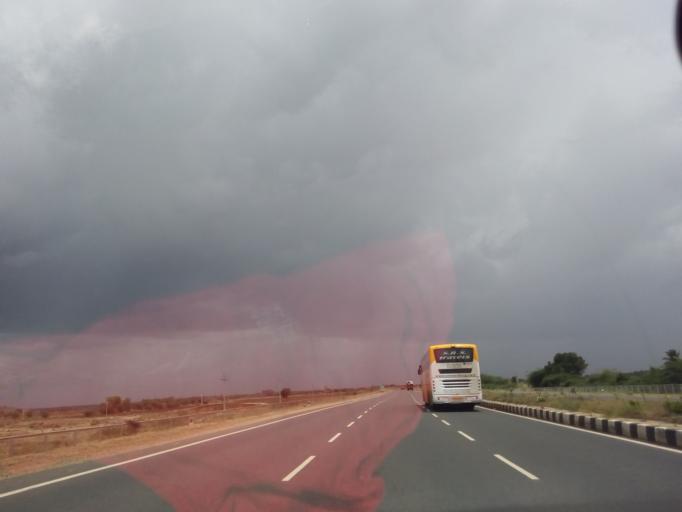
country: IN
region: Karnataka
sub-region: Chitradurga
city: Chitradurga
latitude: 14.1572
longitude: 76.4829
